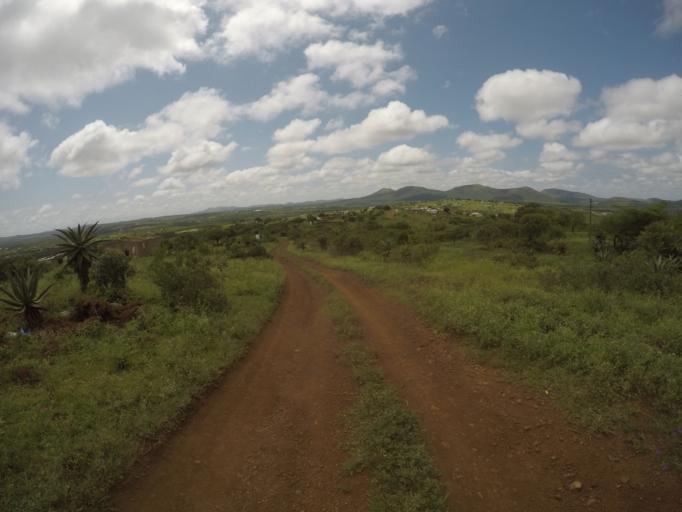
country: ZA
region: KwaZulu-Natal
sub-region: uThungulu District Municipality
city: Empangeni
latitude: -28.5773
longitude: 31.8299
